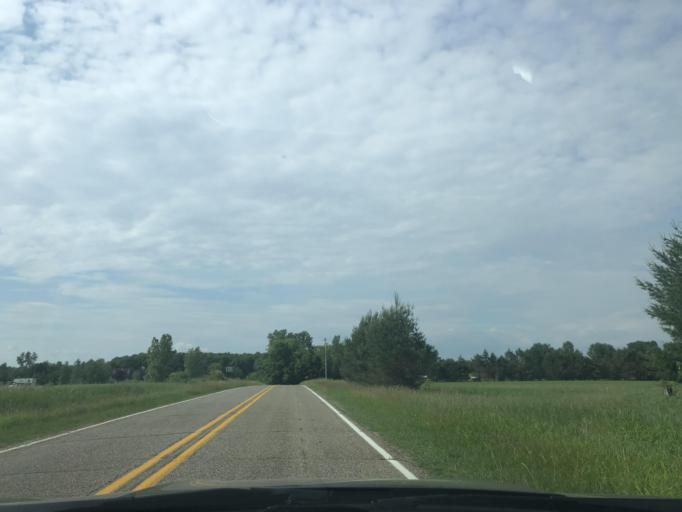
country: US
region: Michigan
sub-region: Clinton County
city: Bath
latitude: 42.8909
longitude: -84.4780
